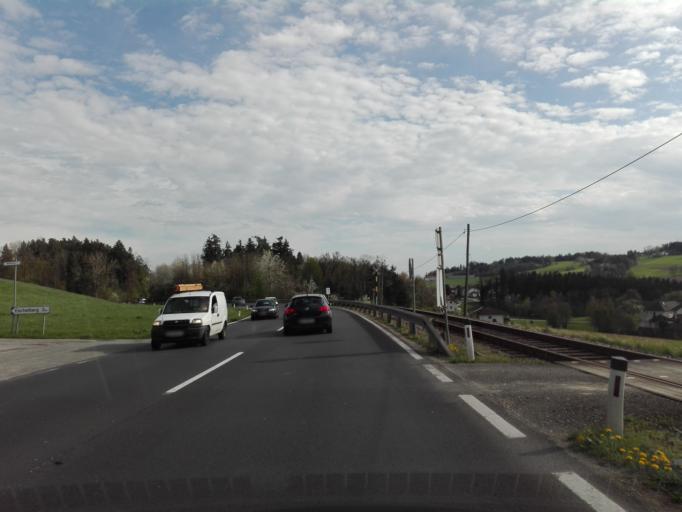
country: AT
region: Upper Austria
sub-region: Politischer Bezirk Urfahr-Umgebung
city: Sankt Gotthard im Muhlkreis
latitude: 48.3887
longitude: 14.0895
